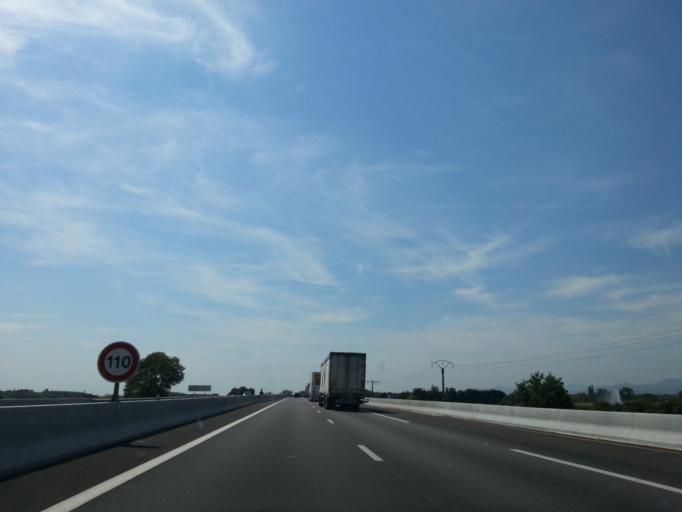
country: FR
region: Alsace
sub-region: Departement du Bas-Rhin
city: Kintzheim
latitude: 48.2275
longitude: 7.4060
